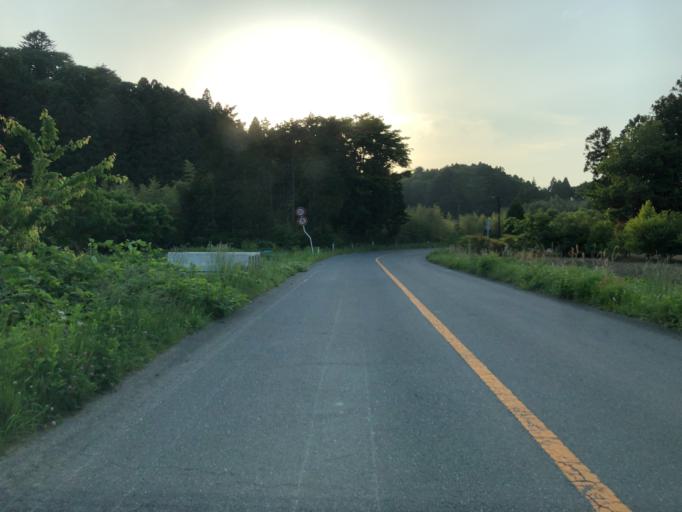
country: JP
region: Fukushima
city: Iwaki
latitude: 37.2123
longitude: 140.9837
